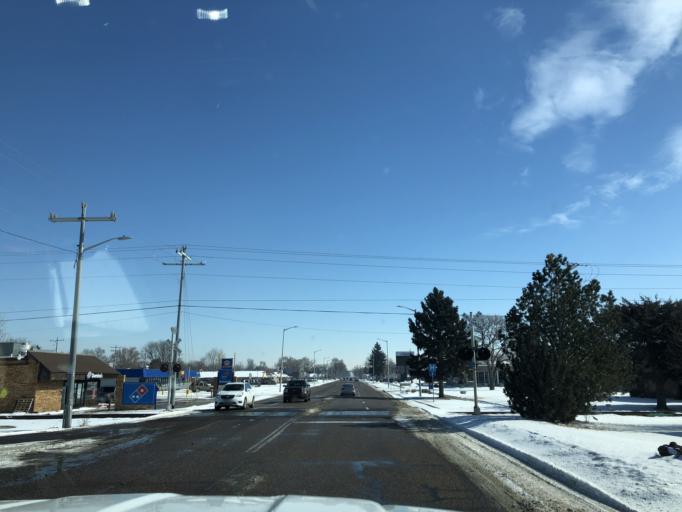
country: US
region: Colorado
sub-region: Morgan County
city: Fort Morgan
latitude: 40.2540
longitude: -103.8162
